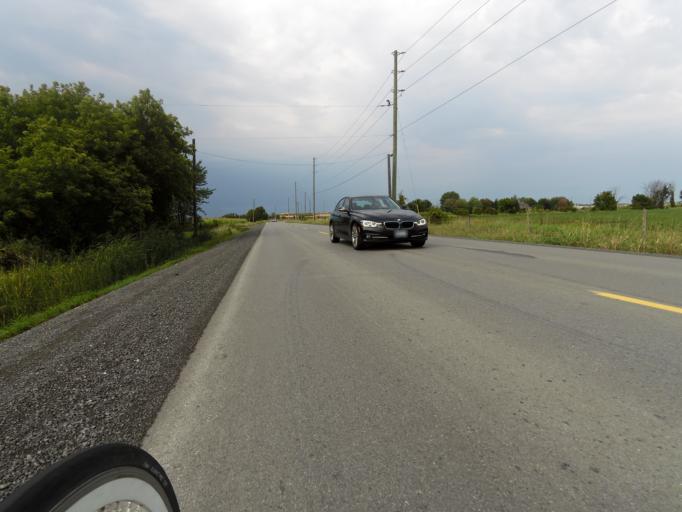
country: CA
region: Ontario
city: Bells Corners
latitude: 45.2555
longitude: -75.7666
